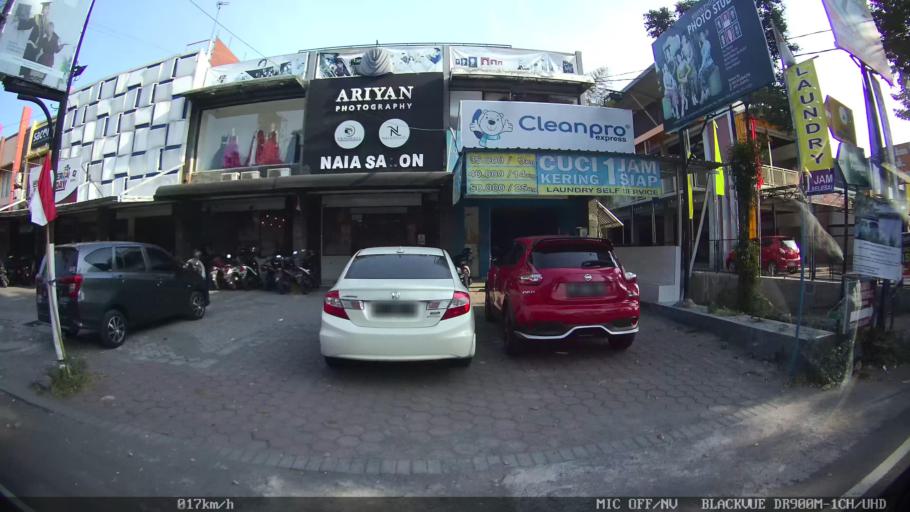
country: ID
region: Daerah Istimewa Yogyakarta
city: Depok
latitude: -7.7743
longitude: 110.4114
